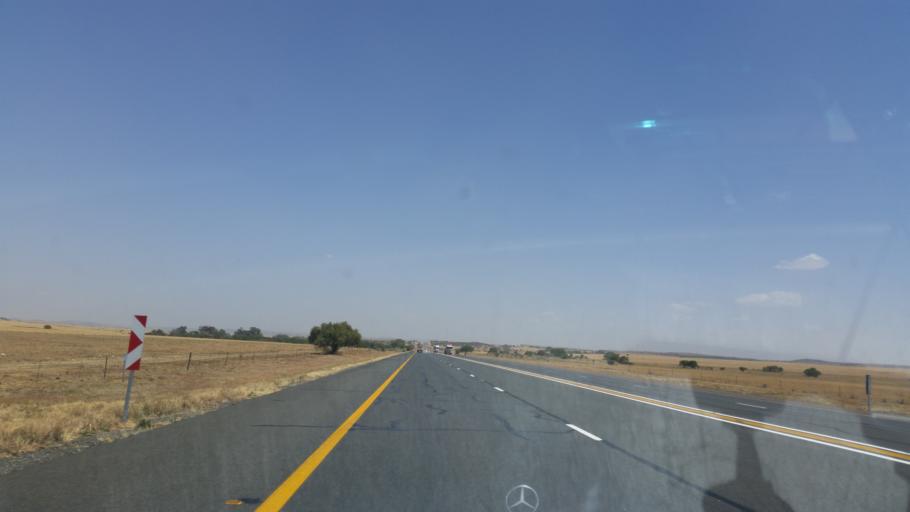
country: ZA
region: Orange Free State
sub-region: Lejweleputswa District Municipality
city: Brandfort
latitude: -28.8908
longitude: 26.4827
